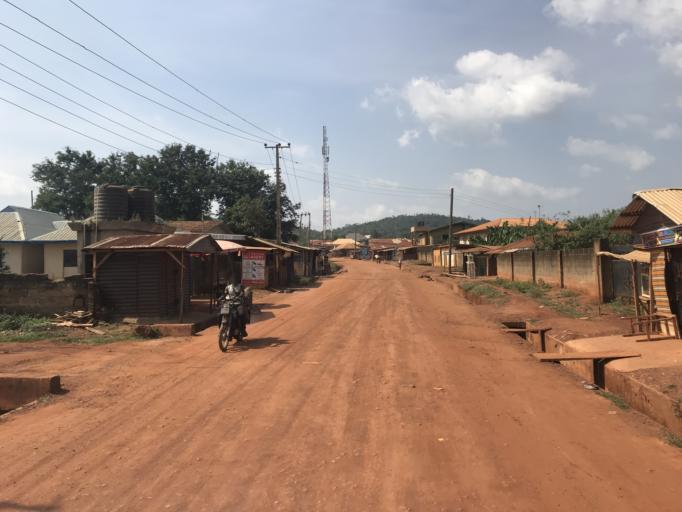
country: NG
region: Osun
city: Ilesa
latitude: 7.6203
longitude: 4.7111
